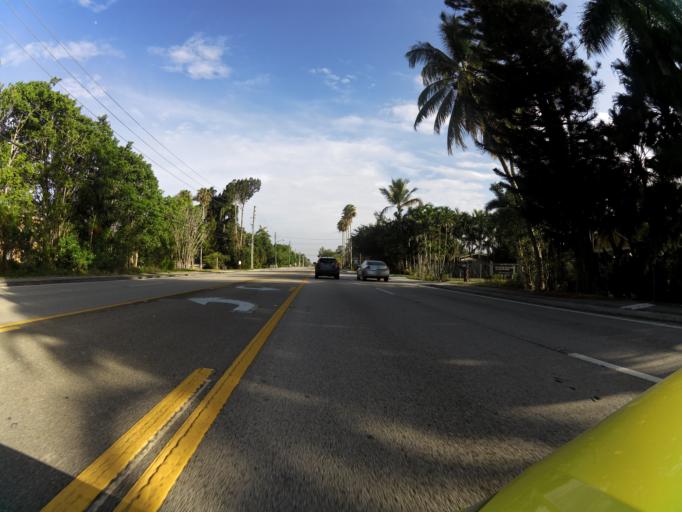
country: US
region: Florida
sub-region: Broward County
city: Davie
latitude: 26.0586
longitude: -80.2320
